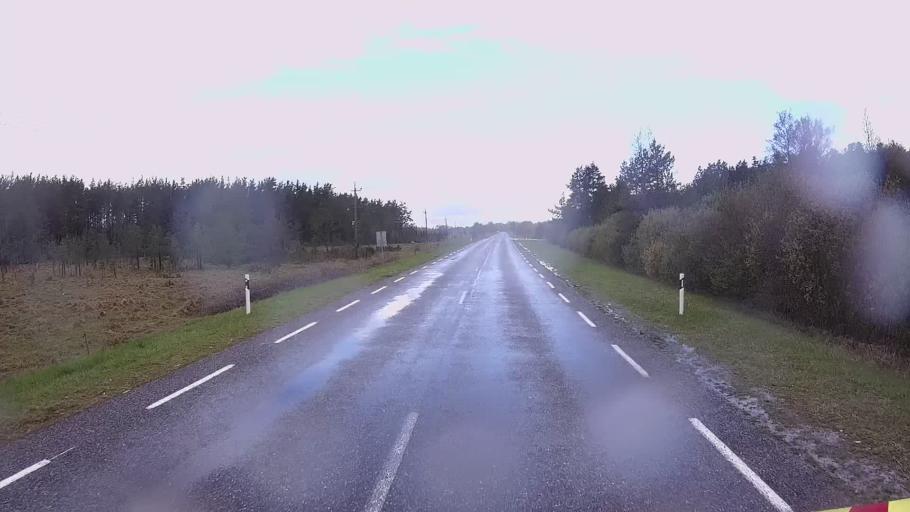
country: EE
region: Hiiumaa
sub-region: Kaerdla linn
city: Kardla
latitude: 58.8327
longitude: 22.8176
